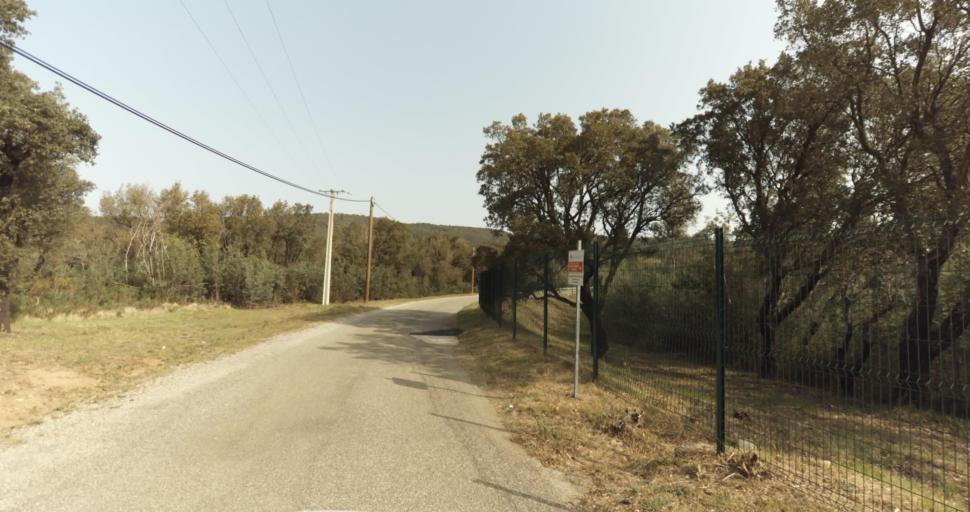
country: FR
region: Provence-Alpes-Cote d'Azur
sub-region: Departement du Var
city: Bormes-les-Mimosas
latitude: 43.1479
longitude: 6.2922
